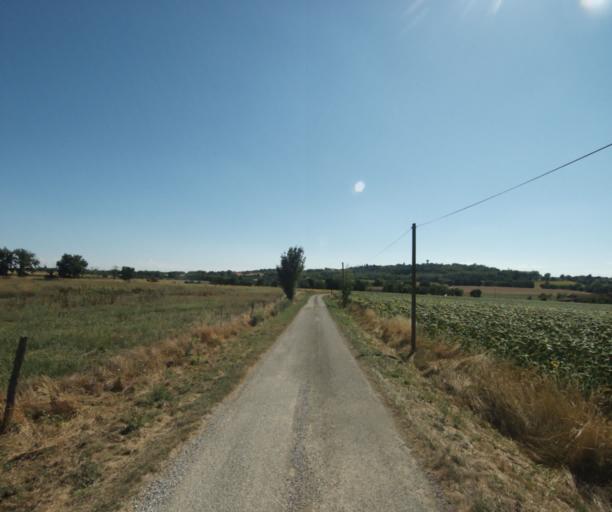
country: FR
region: Midi-Pyrenees
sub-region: Departement de la Haute-Garonne
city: Saint-Felix-Lauragais
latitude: 43.4995
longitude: 1.9118
